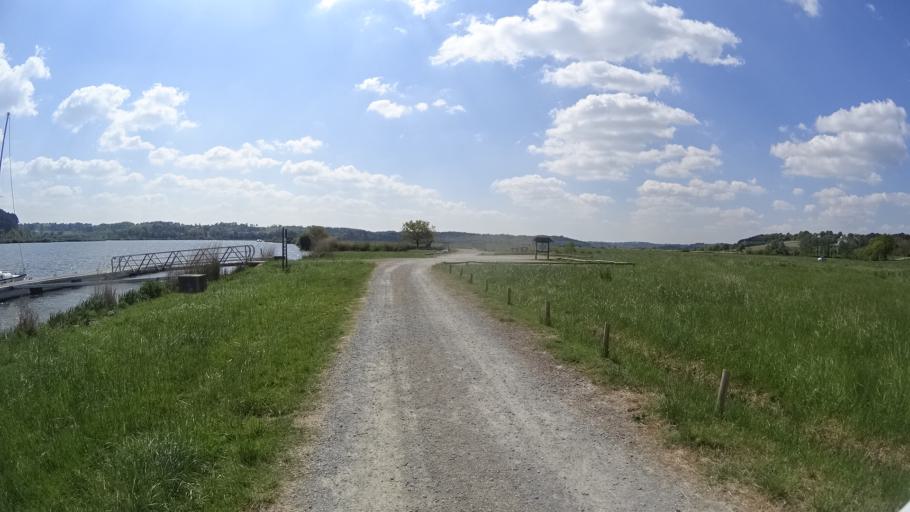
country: FR
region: Brittany
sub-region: Departement du Morbihan
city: Beganne
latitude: 47.5845
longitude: -2.2344
